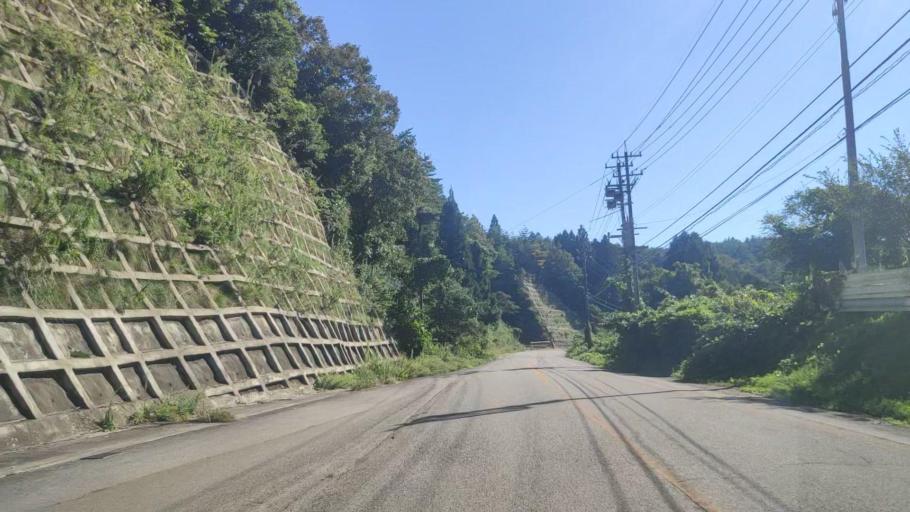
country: JP
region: Ishikawa
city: Nanao
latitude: 37.3175
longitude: 137.1650
